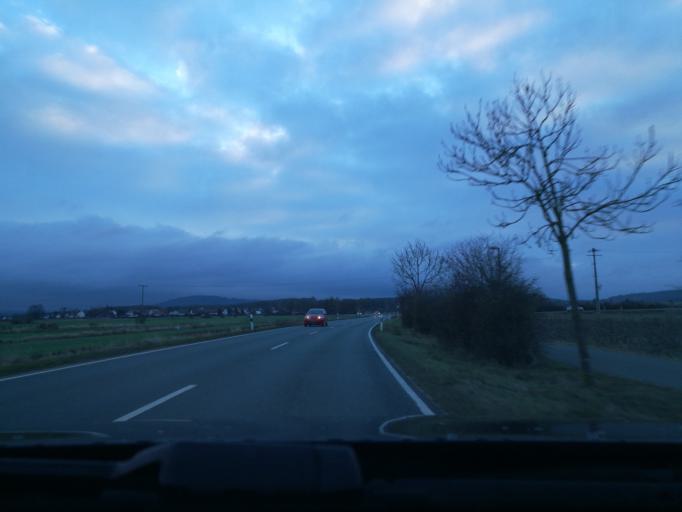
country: DE
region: Bavaria
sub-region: Regierungsbezirk Mittelfranken
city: Baiersdorf
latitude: 49.6568
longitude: 11.0453
